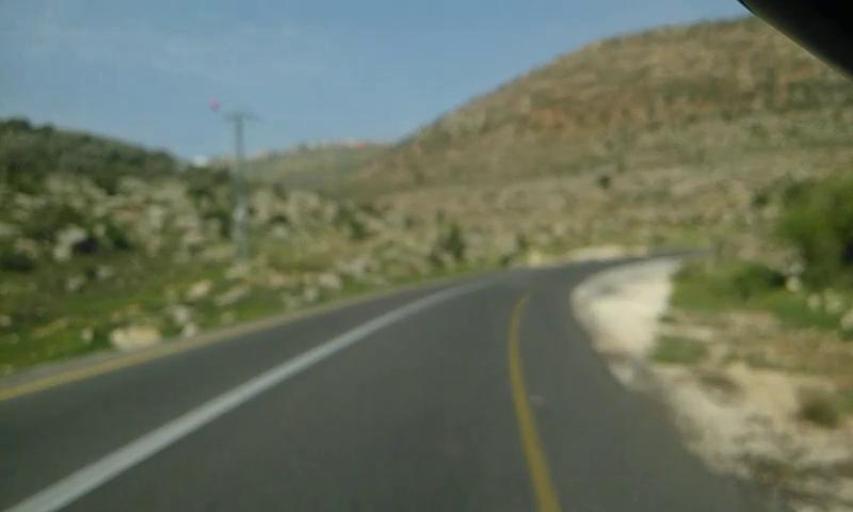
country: PS
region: West Bank
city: `Atarah
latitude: 31.9987
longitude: 35.2239
